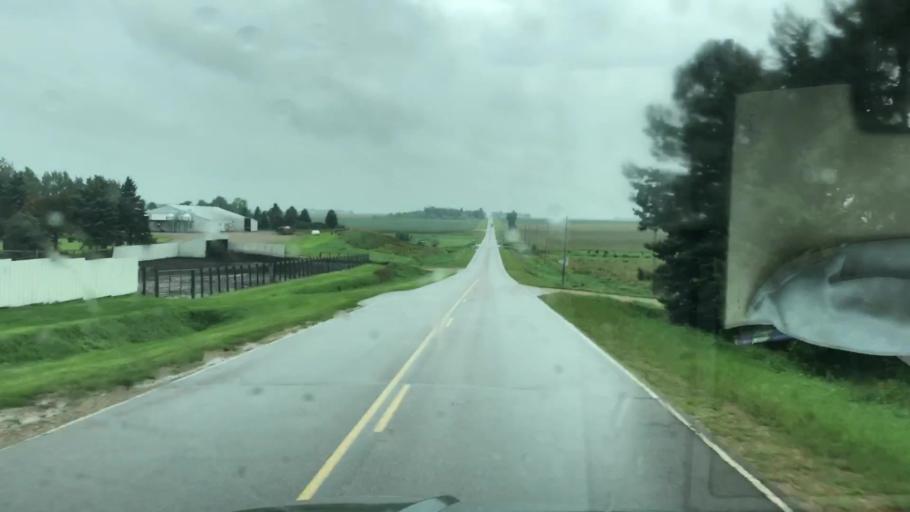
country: US
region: Iowa
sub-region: O'Brien County
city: Sanborn
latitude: 43.2350
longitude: -95.7234
